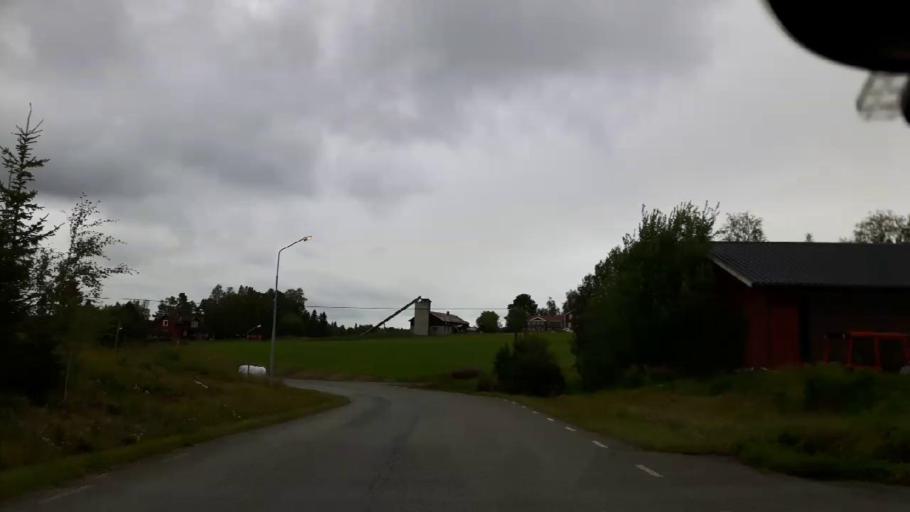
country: SE
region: Jaemtland
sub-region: OEstersunds Kommun
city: Ostersund
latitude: 63.0011
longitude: 14.5828
